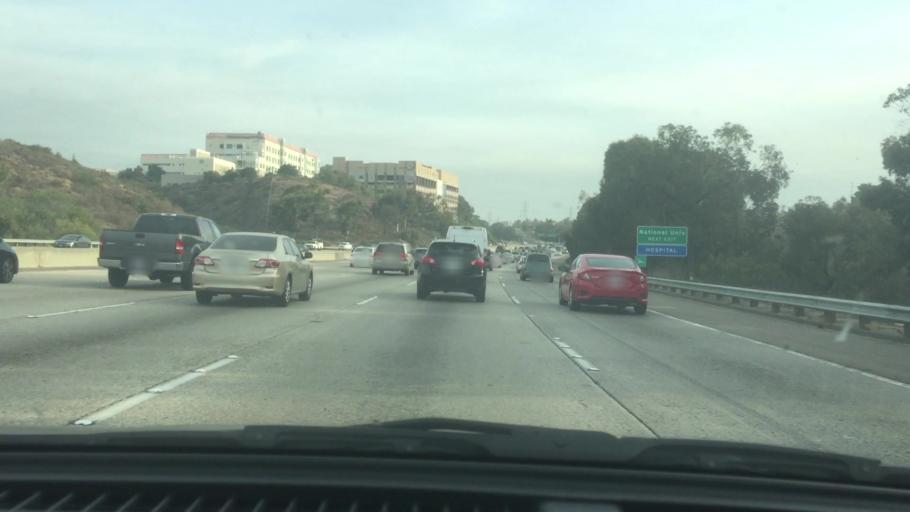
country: US
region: California
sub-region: San Diego County
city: San Diego
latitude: 32.7927
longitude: -117.1492
